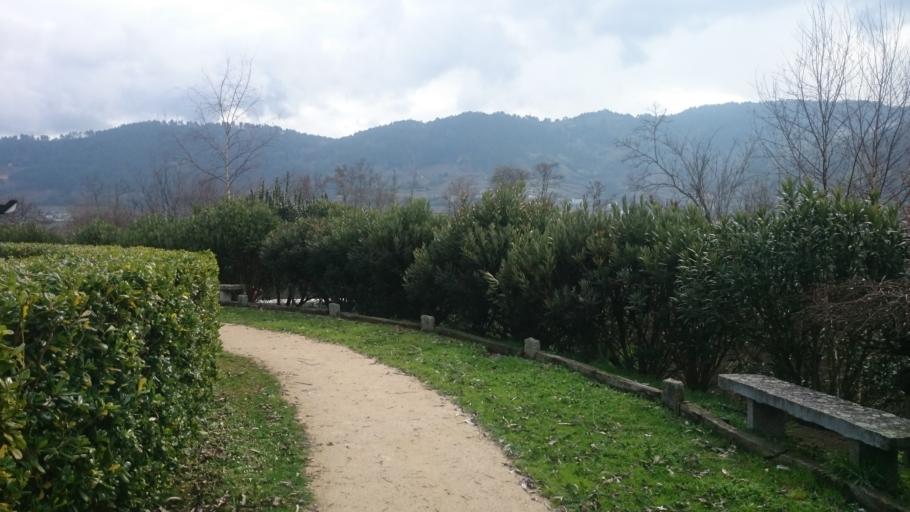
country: ES
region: Galicia
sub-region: Provincia de Ourense
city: Castrelo de Mino
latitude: 42.3256
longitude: -8.0293
